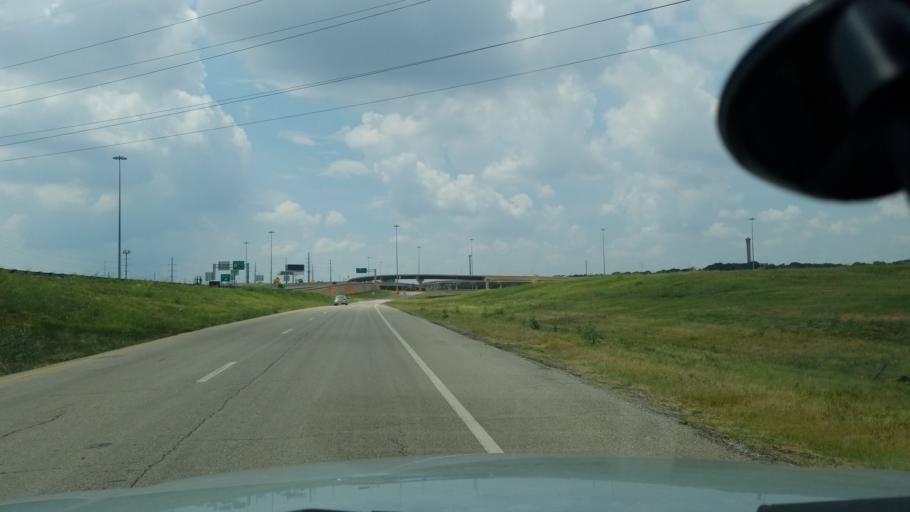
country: US
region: Texas
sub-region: Dallas County
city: Irving
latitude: 32.8513
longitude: -96.9084
